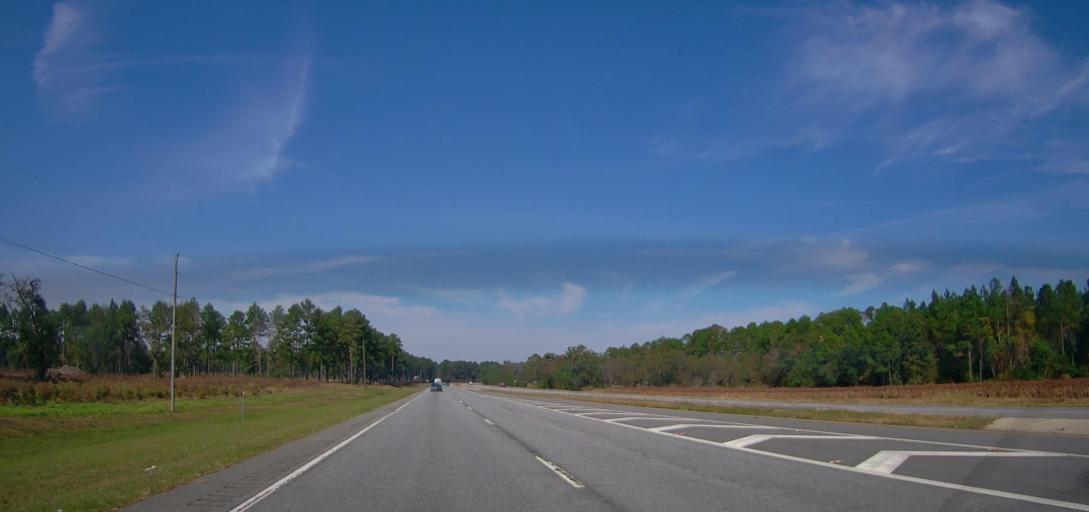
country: US
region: Georgia
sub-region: Lee County
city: Leesburg
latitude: 31.7442
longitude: -83.9874
